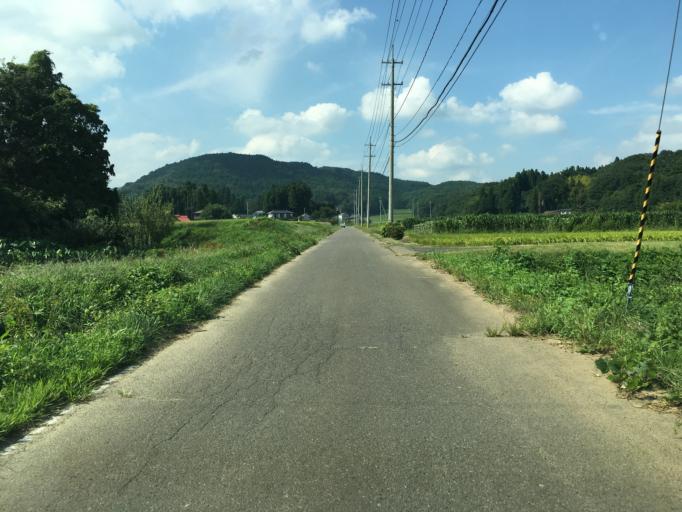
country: JP
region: Fukushima
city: Nihommatsu
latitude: 37.5932
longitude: 140.3865
